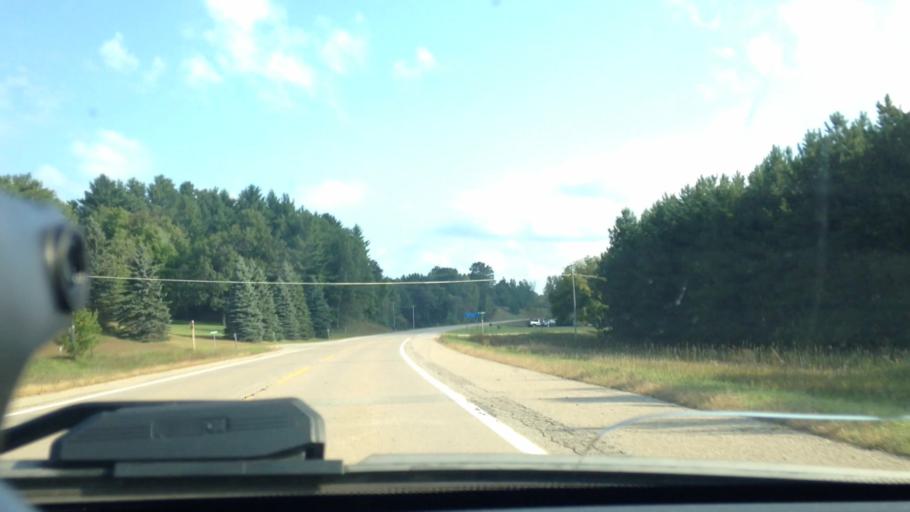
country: US
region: Michigan
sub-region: Dickinson County
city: Norway
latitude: 45.7610
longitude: -87.9210
